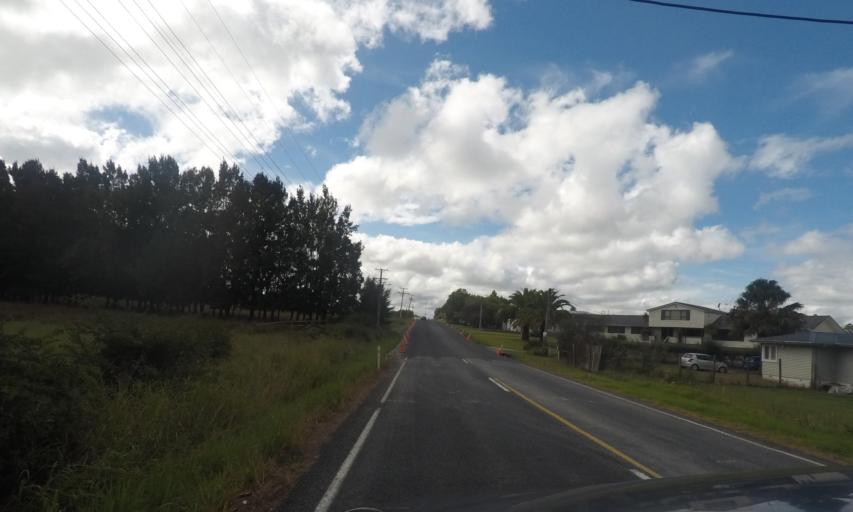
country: NZ
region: Auckland
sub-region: Auckland
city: Rosebank
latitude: -36.7948
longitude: 174.6370
